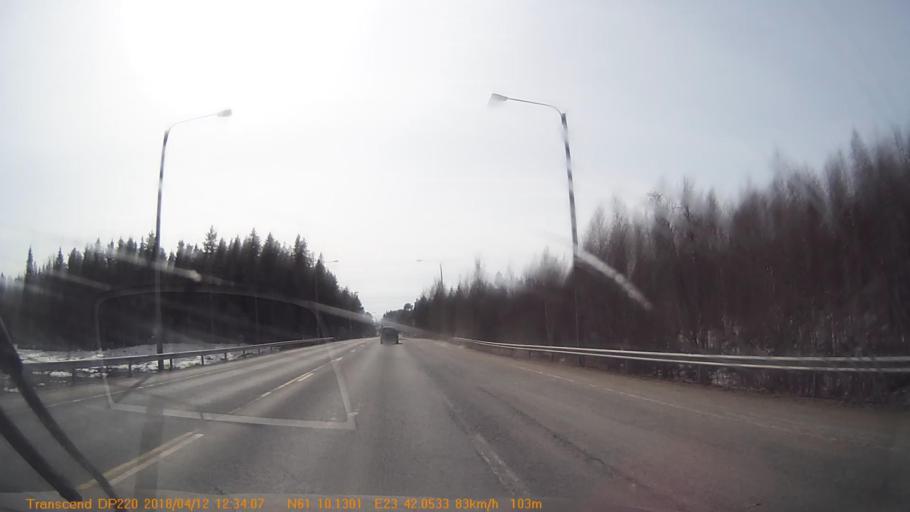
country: FI
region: Pirkanmaa
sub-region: Etelae-Pirkanmaa
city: Kylmaekoski
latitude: 61.1685
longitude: 23.7006
